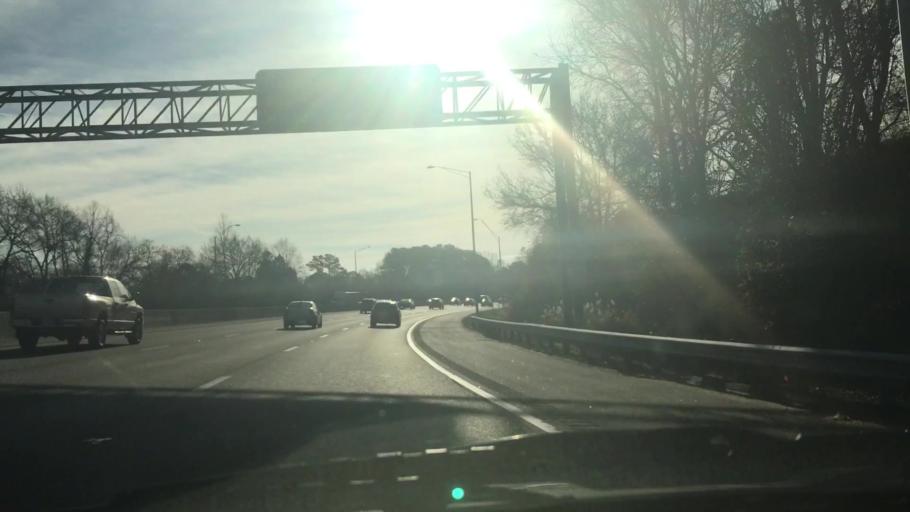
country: US
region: Virginia
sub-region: City of Norfolk
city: Norfolk
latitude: 36.9017
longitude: -76.2366
